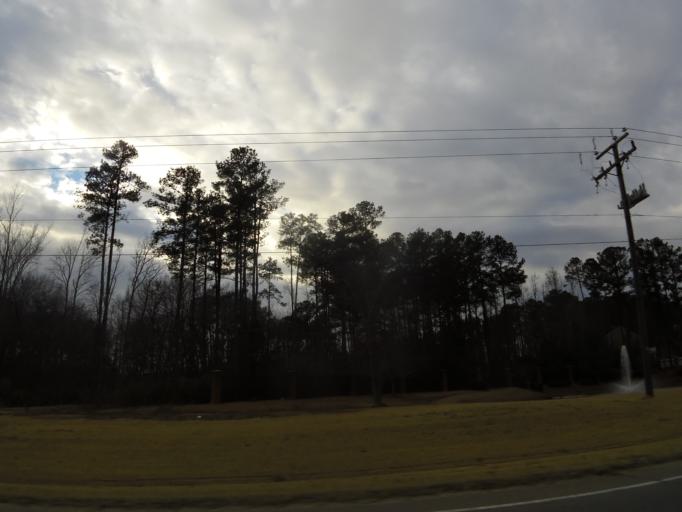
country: US
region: North Carolina
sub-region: Nash County
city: Rocky Mount
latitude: 36.0322
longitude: -77.7666
